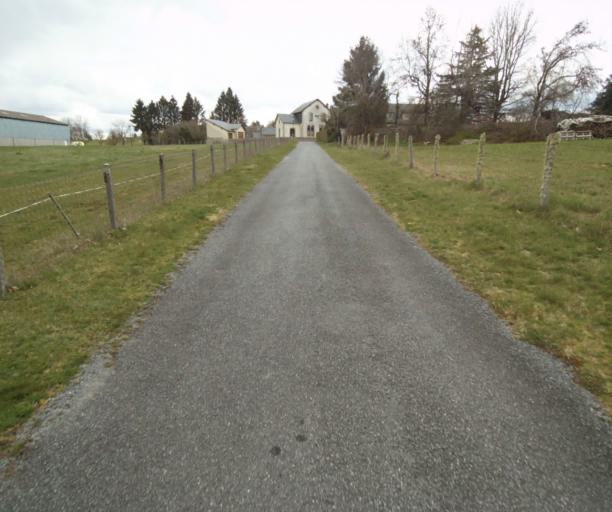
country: FR
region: Limousin
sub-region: Departement de la Correze
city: Correze
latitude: 45.3146
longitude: 1.8876
